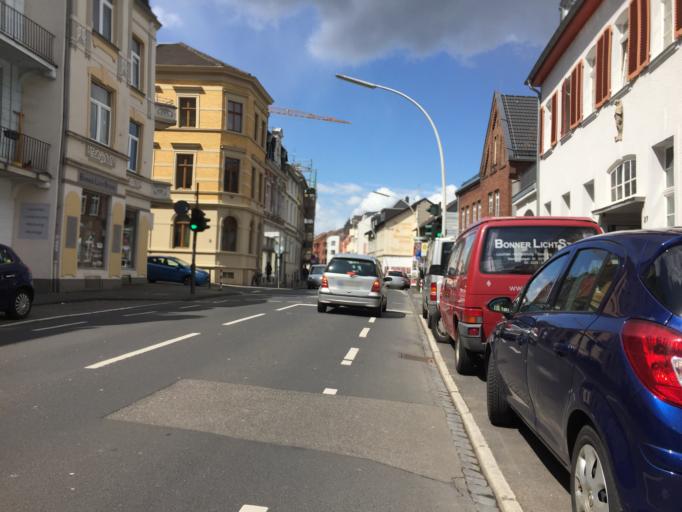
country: DE
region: North Rhine-Westphalia
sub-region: Regierungsbezirk Koln
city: Bonn
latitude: 50.7212
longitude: 7.0908
